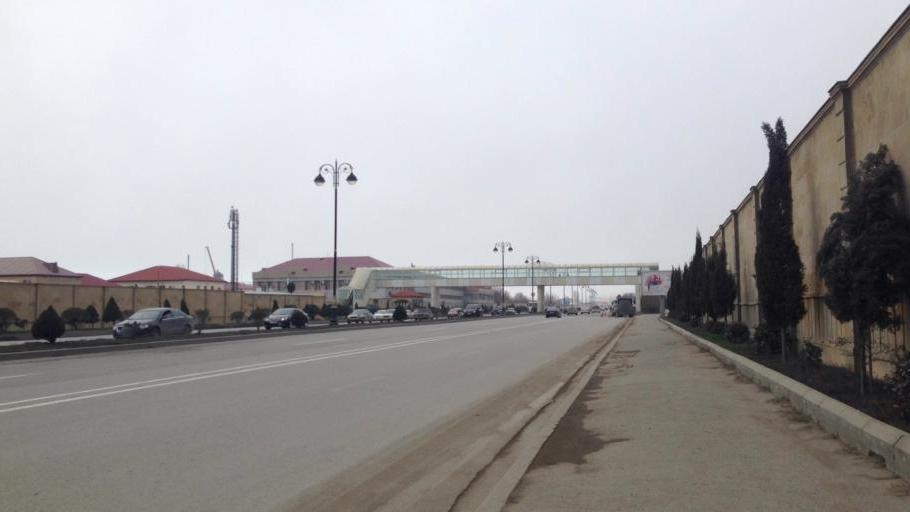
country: AZ
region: Baki
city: Baku
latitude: 40.3771
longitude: 49.9091
